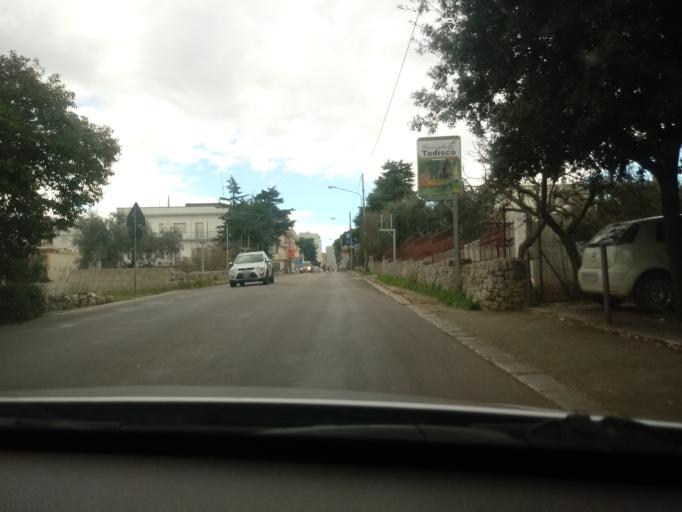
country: IT
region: Apulia
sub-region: Provincia di Bari
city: Putignano
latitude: 40.8551
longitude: 17.1136
